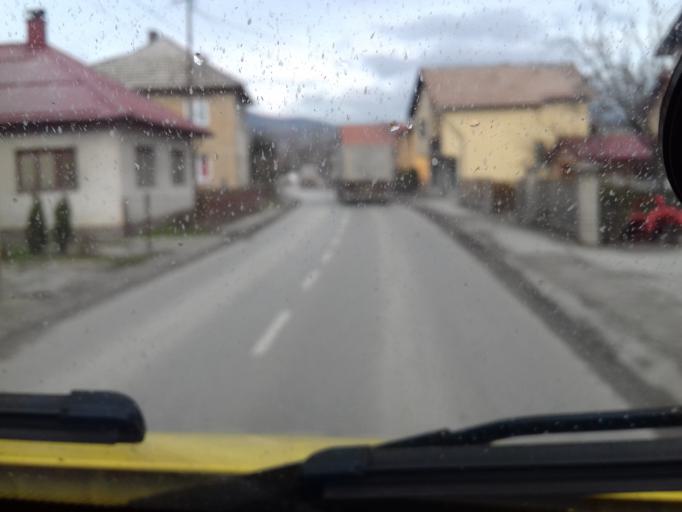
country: BA
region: Federation of Bosnia and Herzegovina
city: Kakanj
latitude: 44.1153
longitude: 18.1170
